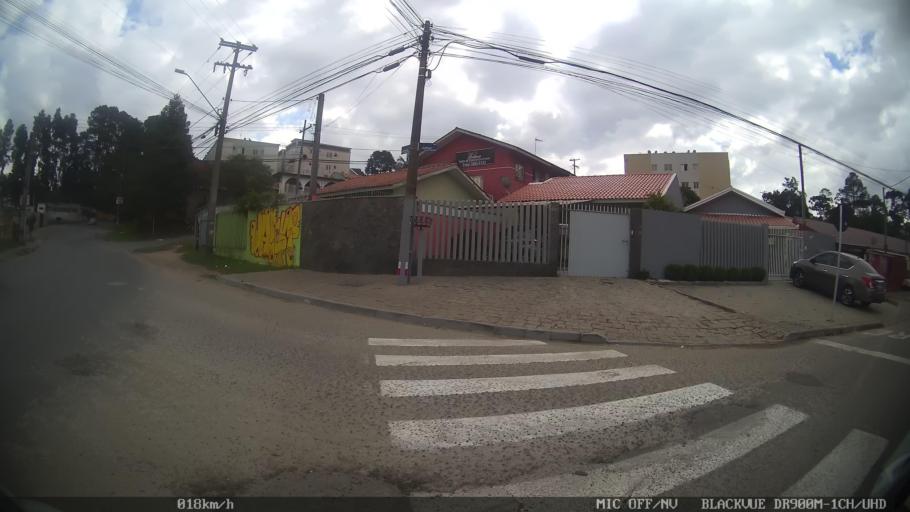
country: BR
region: Parana
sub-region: Colombo
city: Colombo
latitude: -25.3589
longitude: -49.2090
